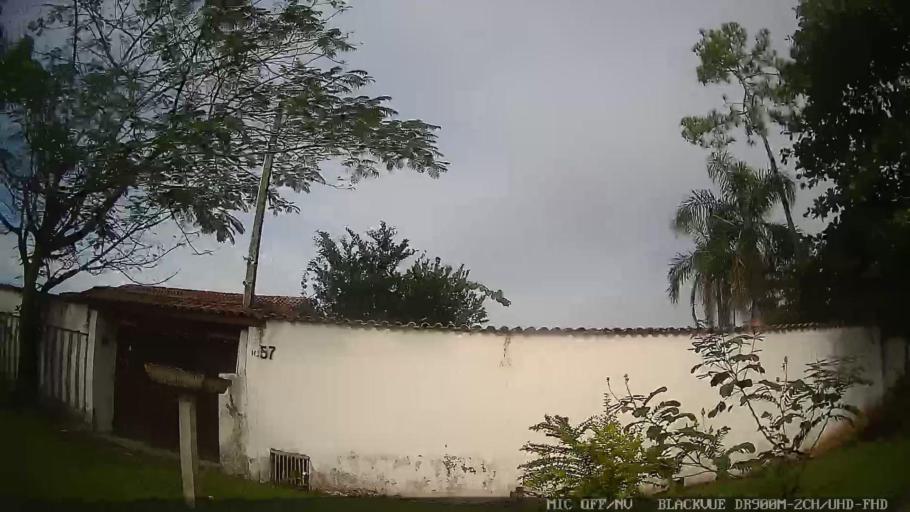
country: BR
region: Sao Paulo
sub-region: Peruibe
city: Peruibe
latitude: -24.2367
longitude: -46.9081
